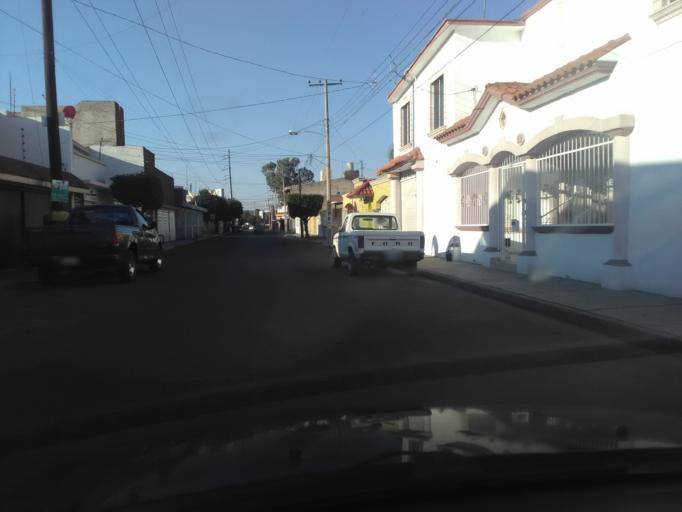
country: MX
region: Durango
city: Victoria de Durango
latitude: 24.0405
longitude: -104.6331
